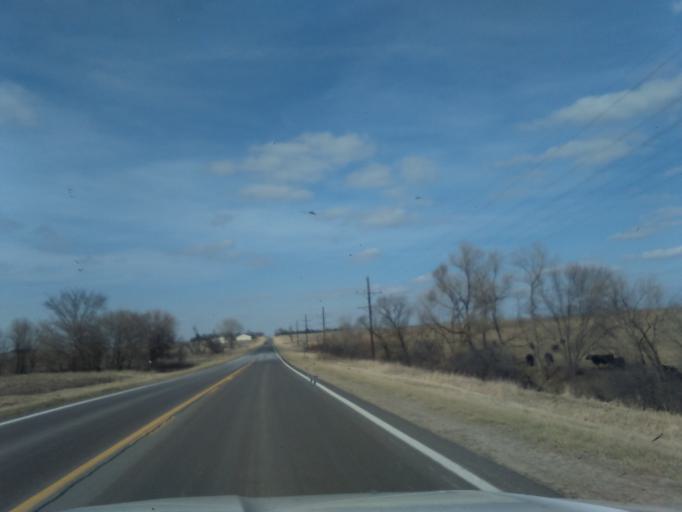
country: US
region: Nebraska
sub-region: Gage County
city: Beatrice
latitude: 40.1207
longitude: -96.9356
